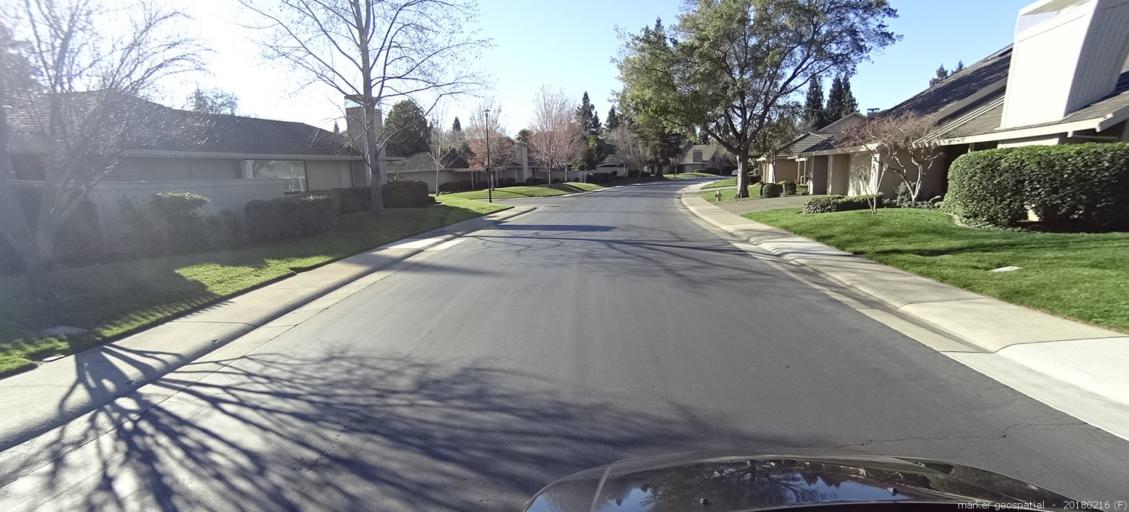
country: US
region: California
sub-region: Sacramento County
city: Gold River
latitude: 38.6265
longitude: -121.2379
